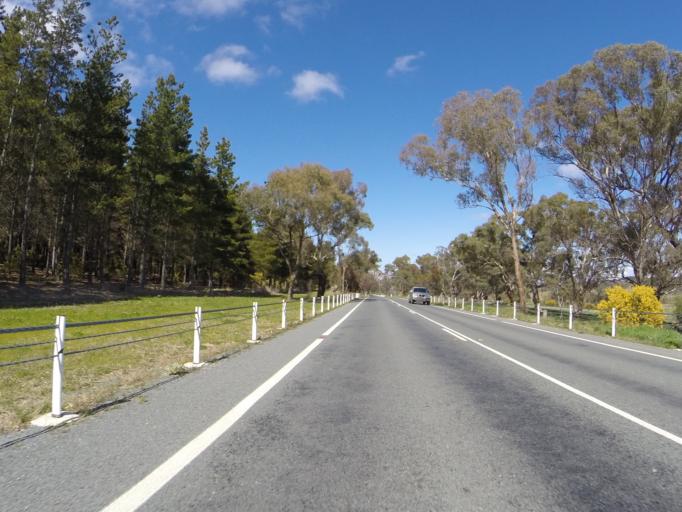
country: AU
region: New South Wales
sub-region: Queanbeyan
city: Queanbeyan
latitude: -35.2978
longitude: 149.2538
